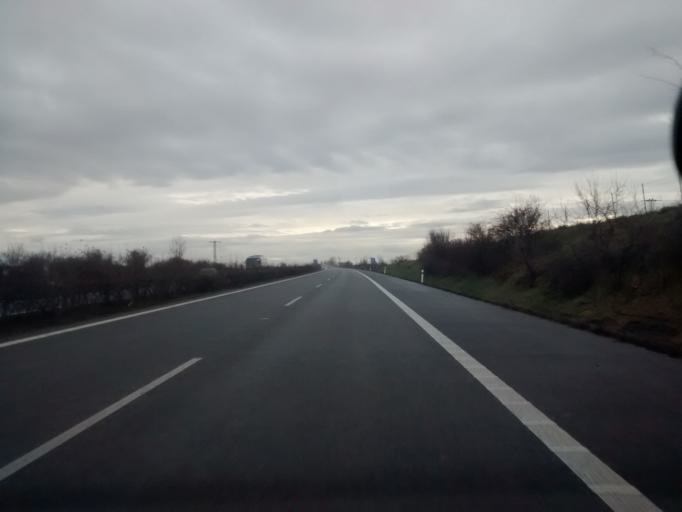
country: CZ
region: Central Bohemia
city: Velvary
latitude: 50.3443
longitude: 14.2793
